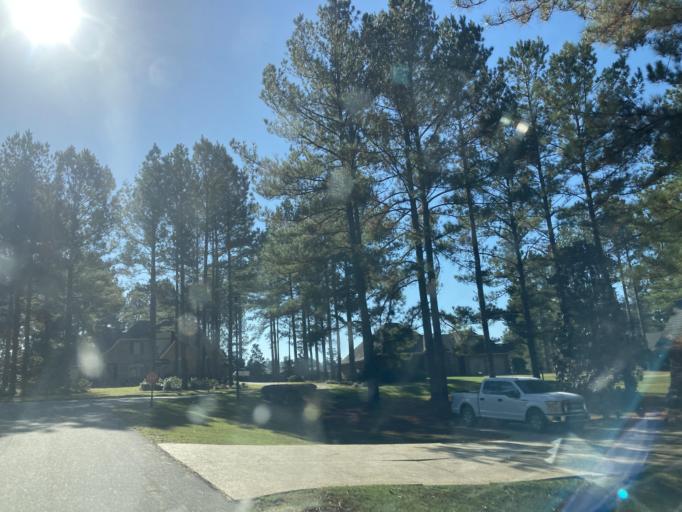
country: US
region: Mississippi
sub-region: Lamar County
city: Sumrall
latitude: 31.3342
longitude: -89.4881
